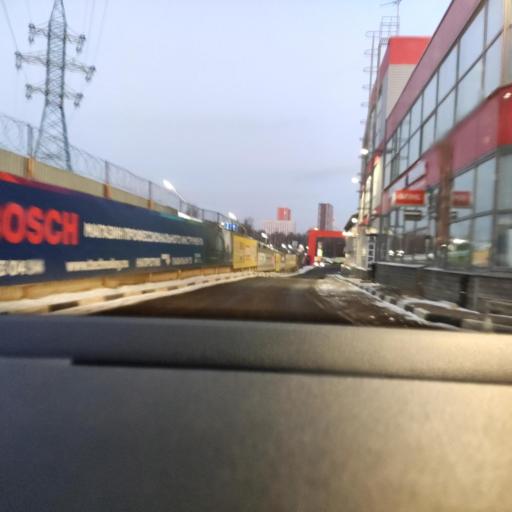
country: RU
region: Moskovskaya
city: Reutov
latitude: 55.7775
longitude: 37.8534
